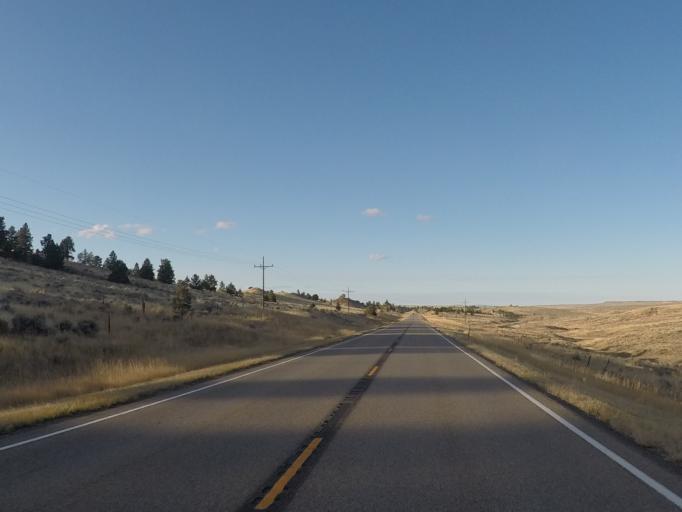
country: US
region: Montana
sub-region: Golden Valley County
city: Ryegate
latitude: 46.2512
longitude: -108.9367
